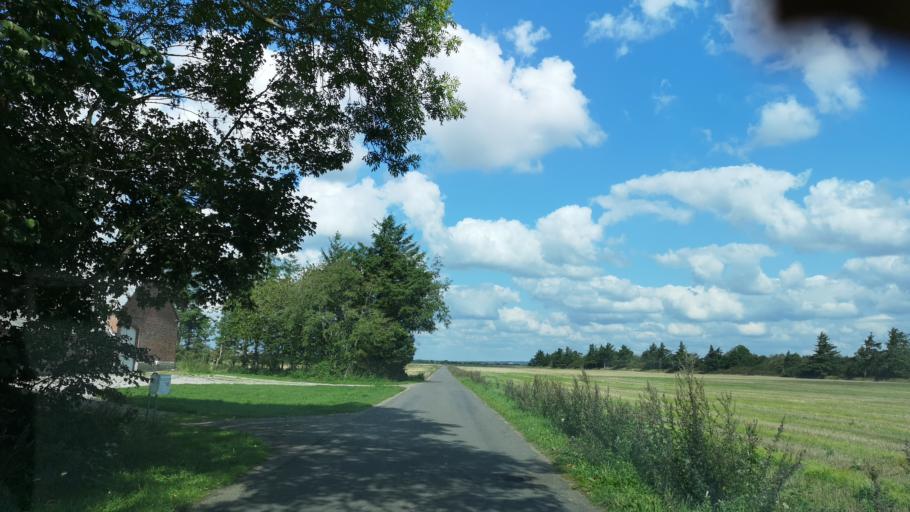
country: DK
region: Central Jutland
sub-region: Ringkobing-Skjern Kommune
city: Skjern
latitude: 55.8980
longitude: 8.4013
